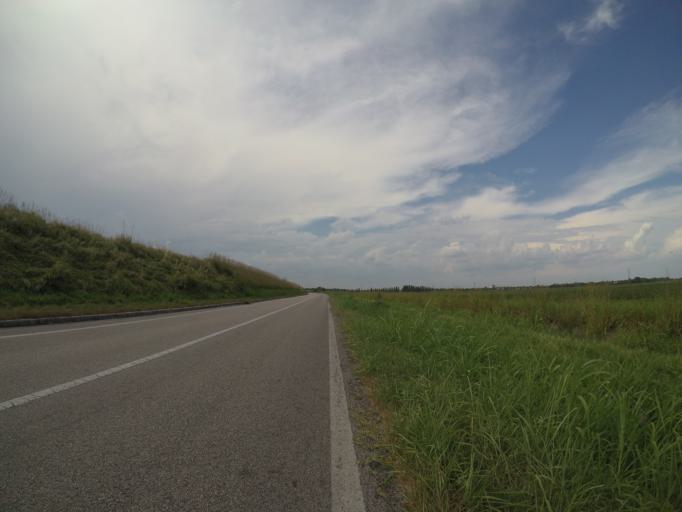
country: IT
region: Friuli Venezia Giulia
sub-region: Provincia di Udine
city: Pertegada
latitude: 45.6783
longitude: 13.0658
